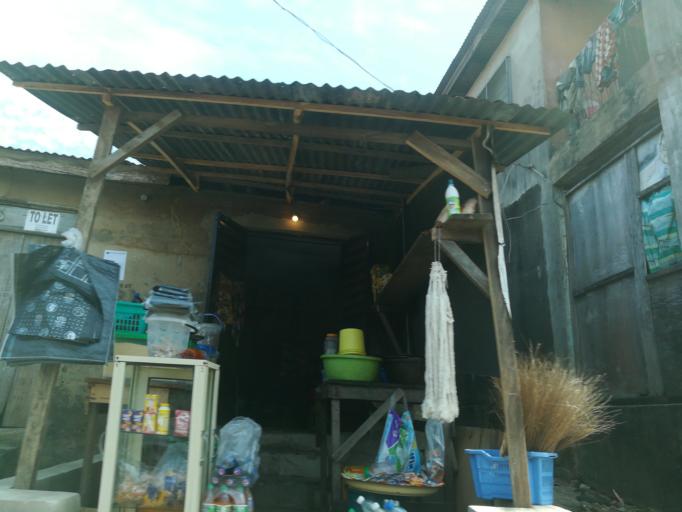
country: NG
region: Lagos
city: Ikorodu
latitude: 6.6231
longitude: 3.4949
